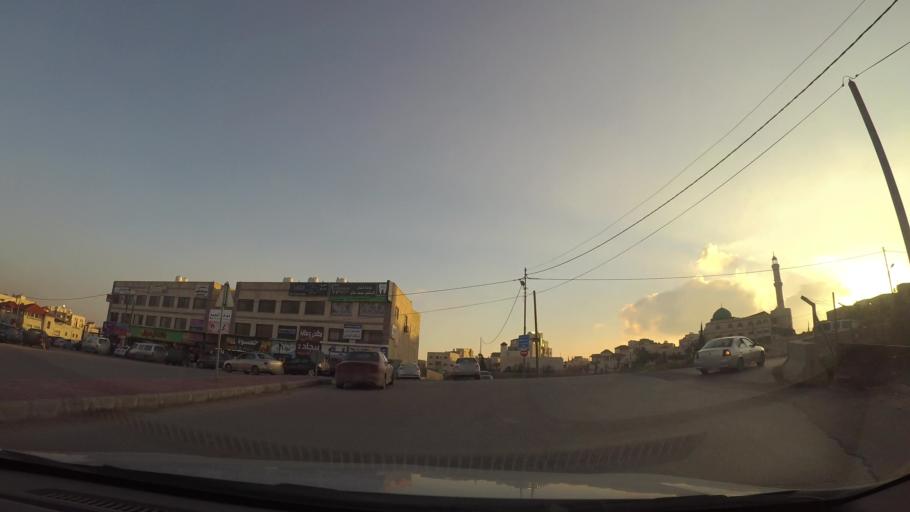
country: JO
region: Amman
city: Al Bunayyat ash Shamaliyah
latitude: 31.9049
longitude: 35.9202
